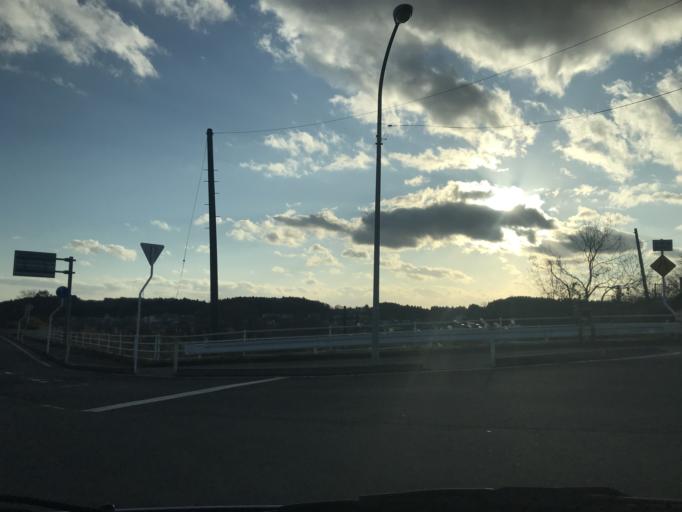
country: JP
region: Miyagi
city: Kogota
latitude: 38.6675
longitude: 141.0718
